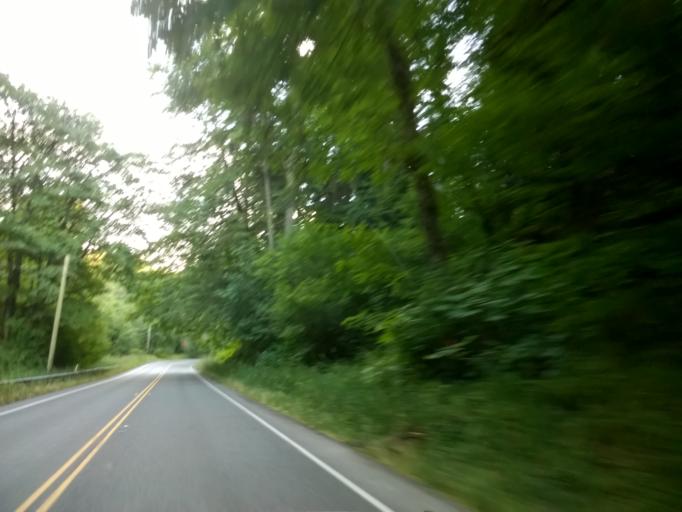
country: US
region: Washington
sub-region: King County
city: Duvall
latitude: 47.7492
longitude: -122.0151
